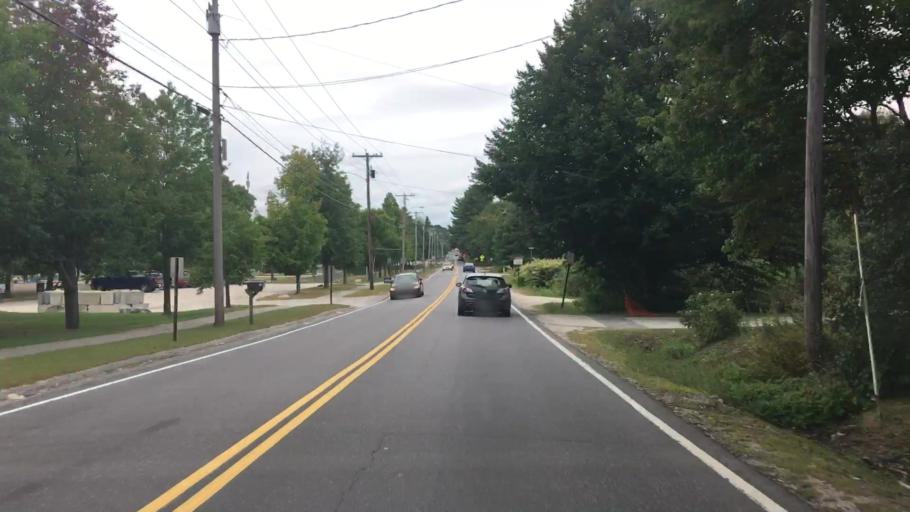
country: US
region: Maine
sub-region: Cumberland County
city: Yarmouth
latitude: 43.8091
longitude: -70.1760
